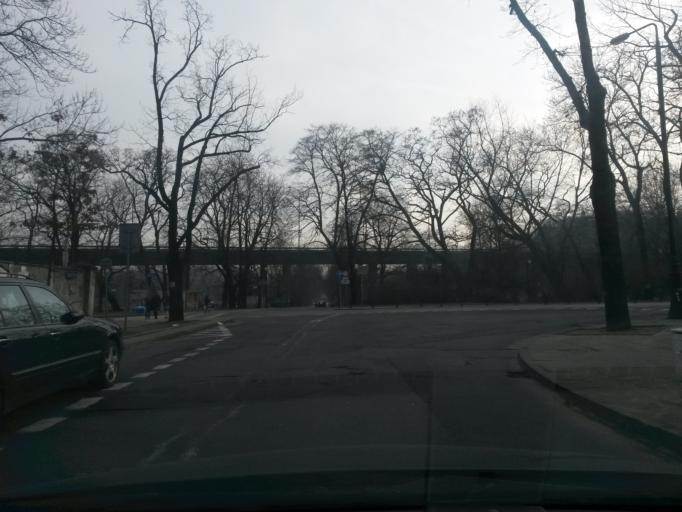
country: PL
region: Masovian Voivodeship
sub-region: Warszawa
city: Srodmiescie
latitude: 52.2224
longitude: 21.0333
